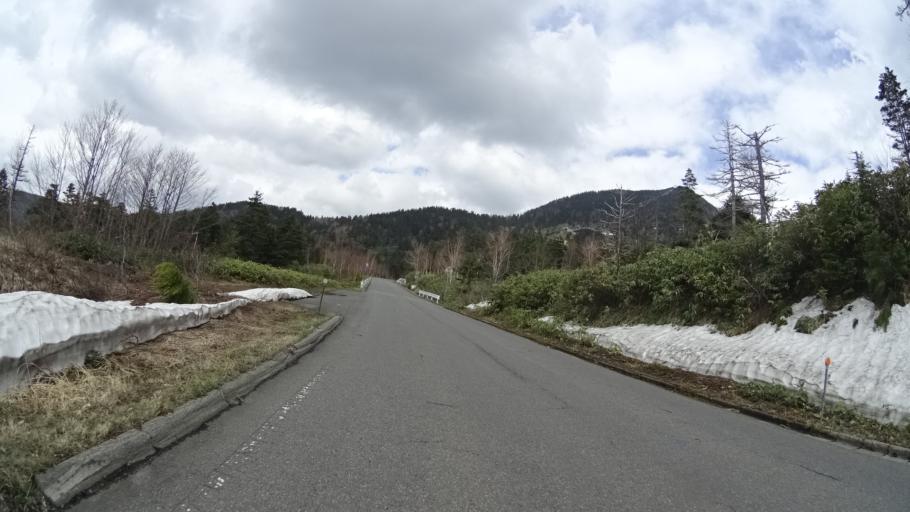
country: JP
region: Nagano
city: Nakano
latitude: 36.6705
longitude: 138.5123
